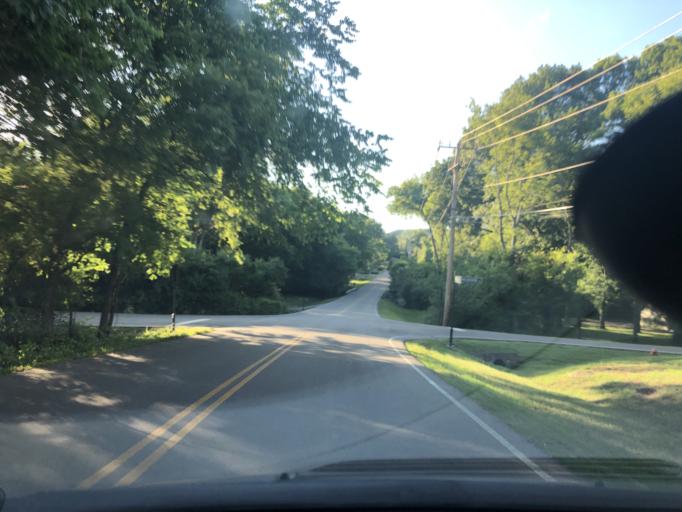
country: US
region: Tennessee
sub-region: Davidson County
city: Forest Hills
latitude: 36.0545
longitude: -86.8492
